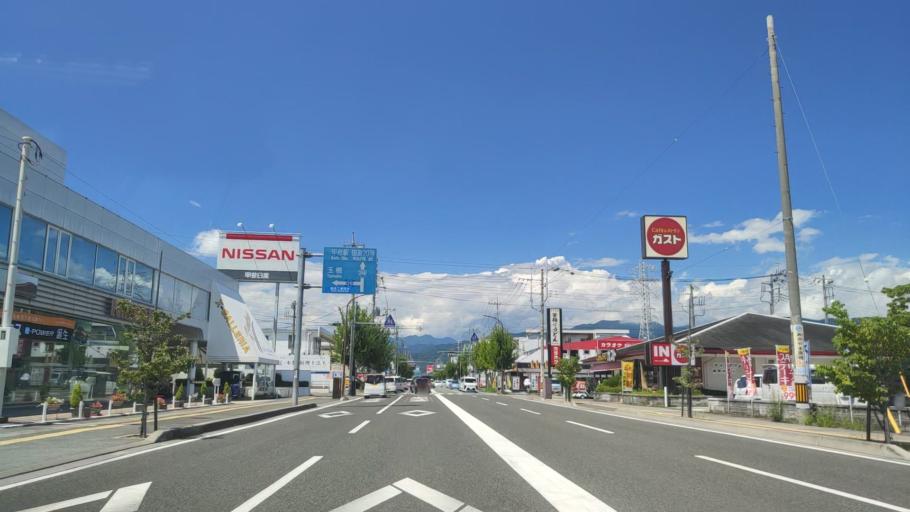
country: JP
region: Yamanashi
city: Kofu-shi
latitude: 35.6253
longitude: 138.5719
